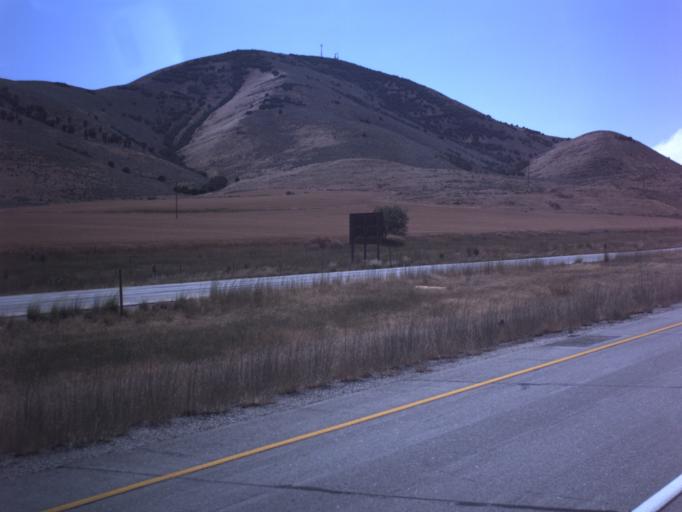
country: US
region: Utah
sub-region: Box Elder County
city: Garland
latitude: 41.8014
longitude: -112.3092
